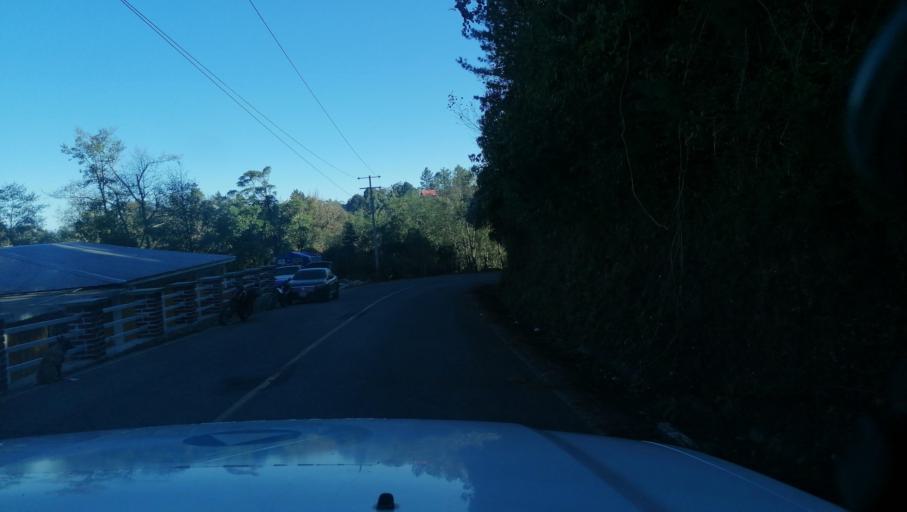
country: MX
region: Chiapas
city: Motozintla de Mendoza
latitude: 15.2470
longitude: -92.2295
